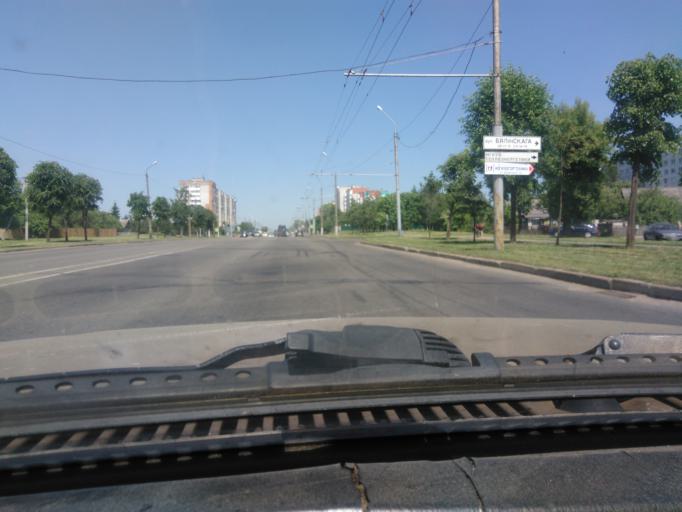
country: BY
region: Mogilev
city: Mahilyow
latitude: 53.9301
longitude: 30.3514
